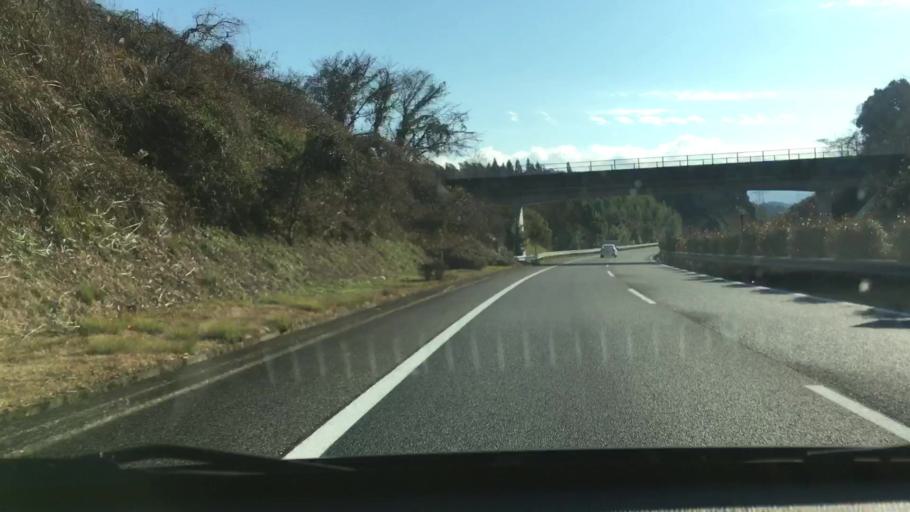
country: JP
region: Kumamoto
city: Hitoyoshi
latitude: 32.2191
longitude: 130.7803
